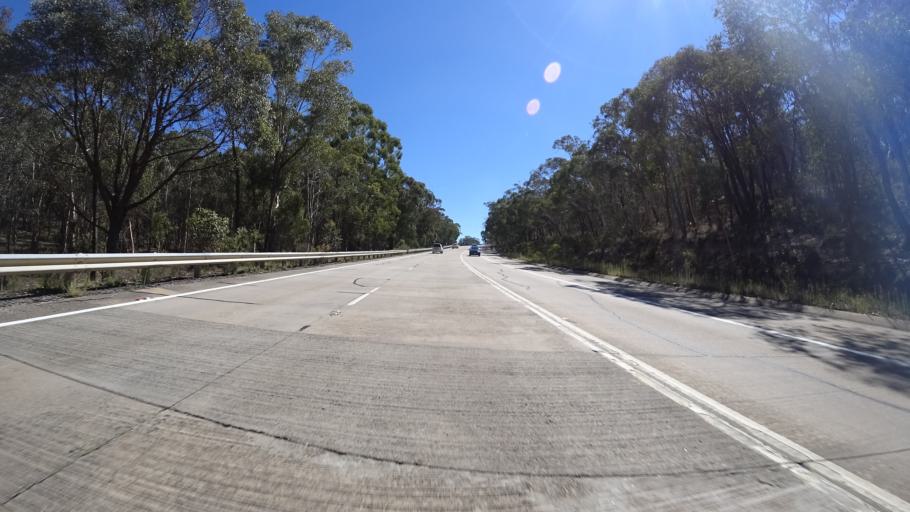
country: AU
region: New South Wales
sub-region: Lithgow
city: Portland
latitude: -33.3390
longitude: 150.0360
